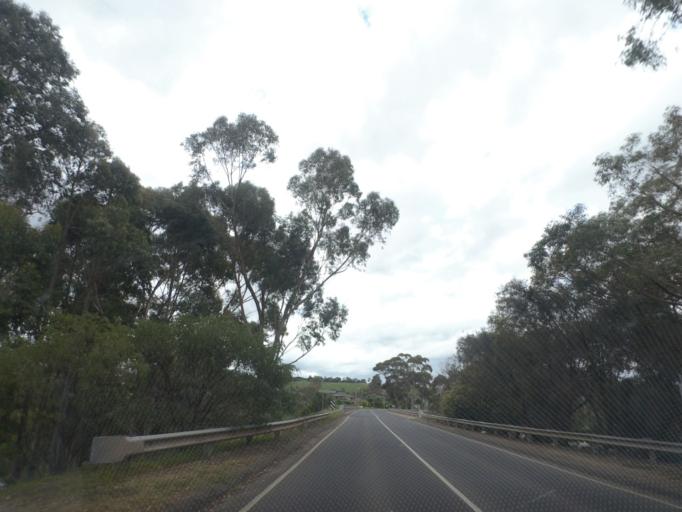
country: AU
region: Victoria
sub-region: Brimbank
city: Keilor
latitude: -37.7050
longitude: 144.8325
